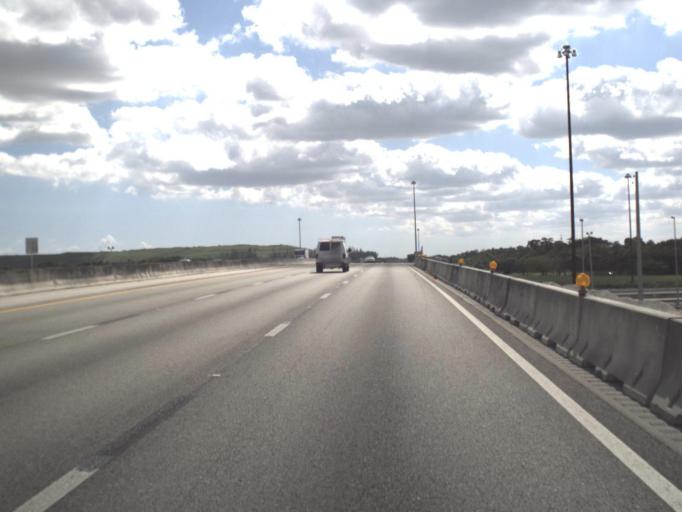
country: US
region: Florida
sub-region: Palm Beach County
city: Boca Pointe
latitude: 26.3069
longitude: -80.1697
